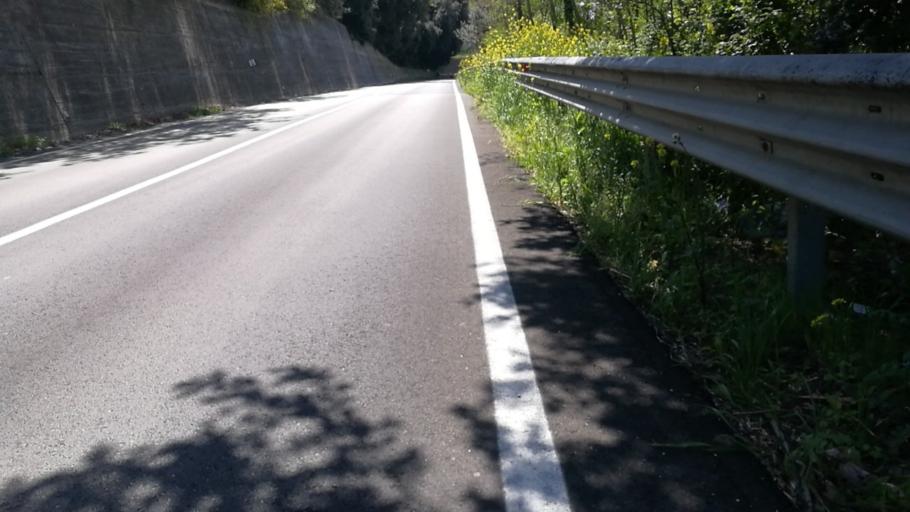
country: IT
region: Abruzzo
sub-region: Provincia di Chieti
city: Marina di San Vito
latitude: 42.2998
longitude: 14.4420
